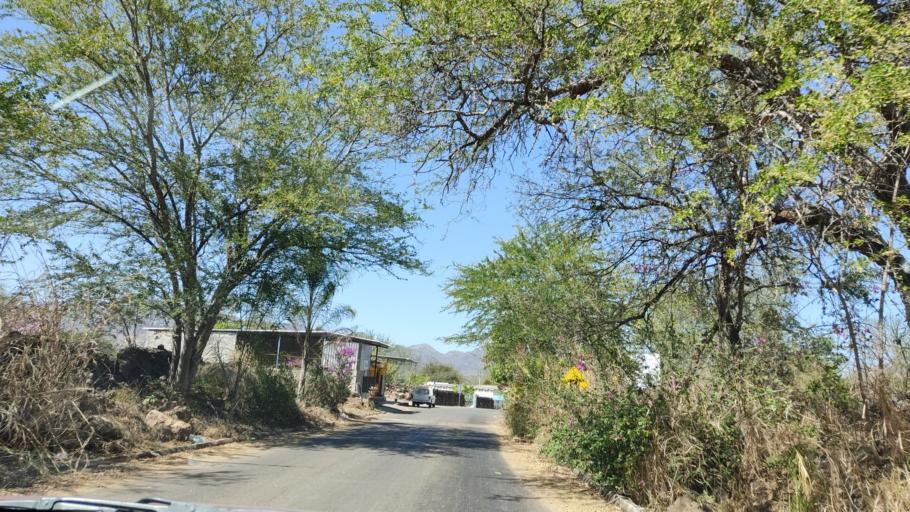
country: MX
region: Nayarit
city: Santa Maria del Oro
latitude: 21.4994
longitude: -104.6217
